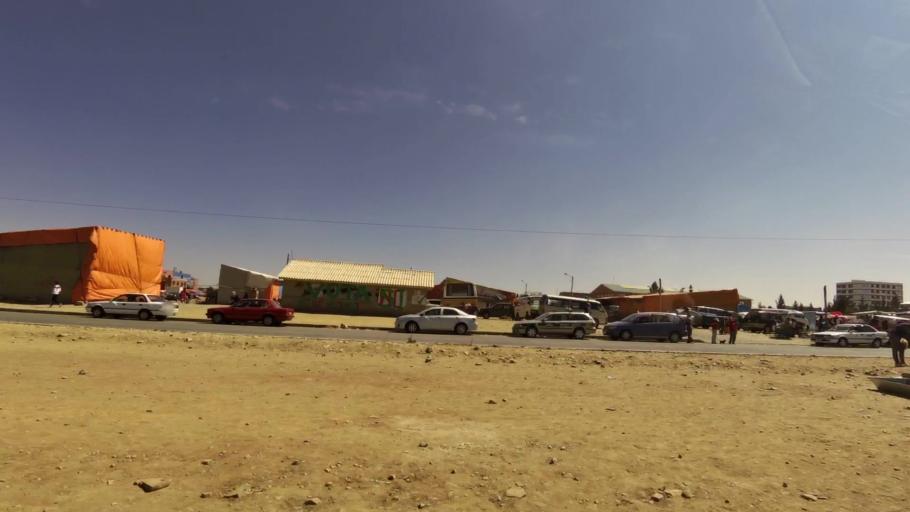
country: BO
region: La Paz
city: La Paz
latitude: -16.5379
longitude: -68.1662
